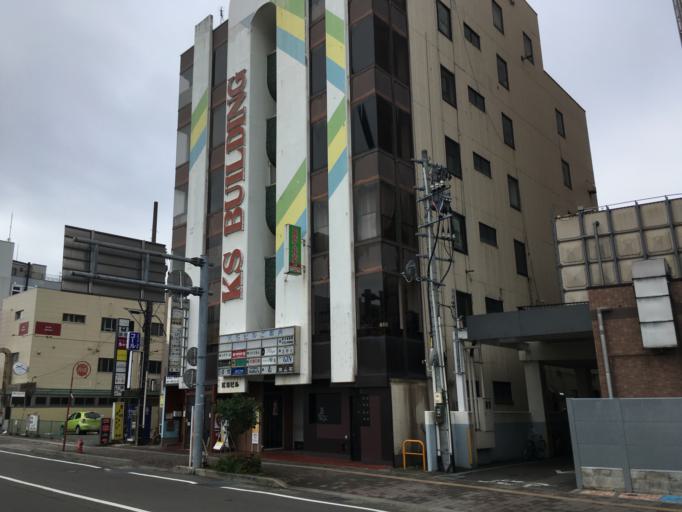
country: JP
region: Akita
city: Akita
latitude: 39.7159
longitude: 140.1285
